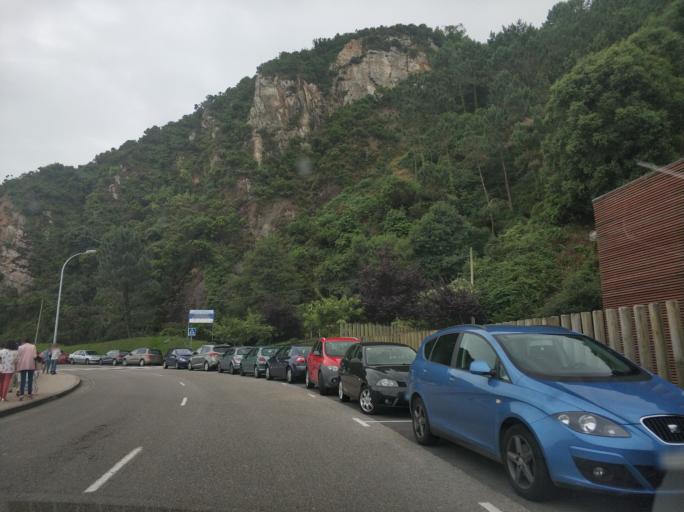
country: ES
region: Asturias
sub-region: Province of Asturias
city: Cudillero
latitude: 43.5649
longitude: -6.1497
